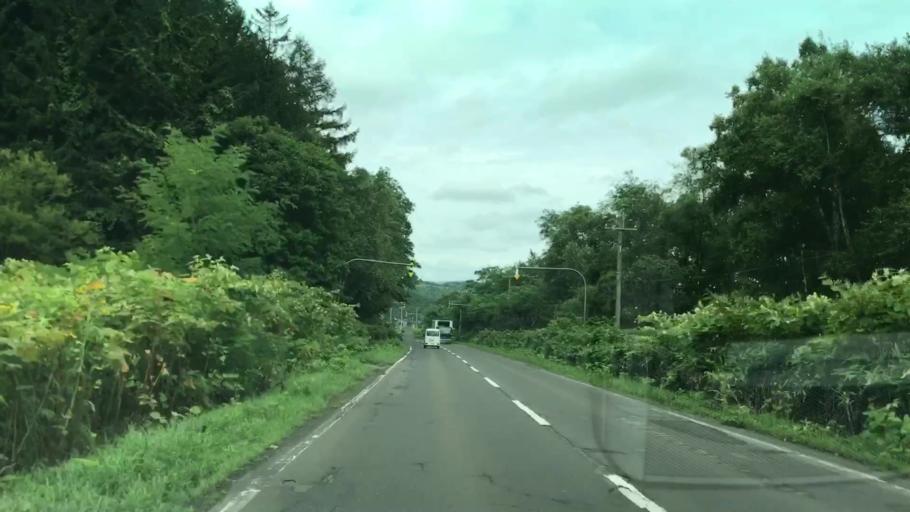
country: JP
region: Hokkaido
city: Niseko Town
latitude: 42.9555
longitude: 140.6965
